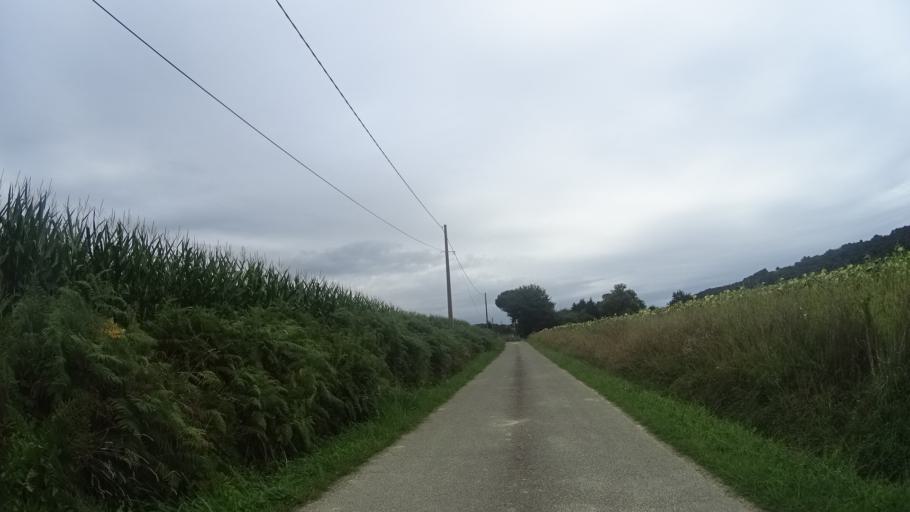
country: FR
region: Aquitaine
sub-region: Departement des Pyrenees-Atlantiques
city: Orthez
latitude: 43.4917
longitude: -0.7115
